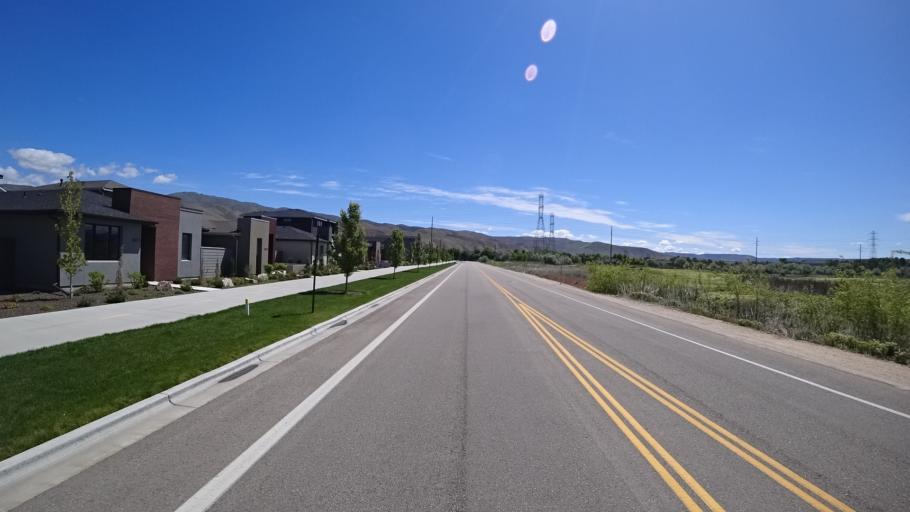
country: US
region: Idaho
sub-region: Ada County
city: Boise
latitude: 43.5665
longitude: -116.1287
